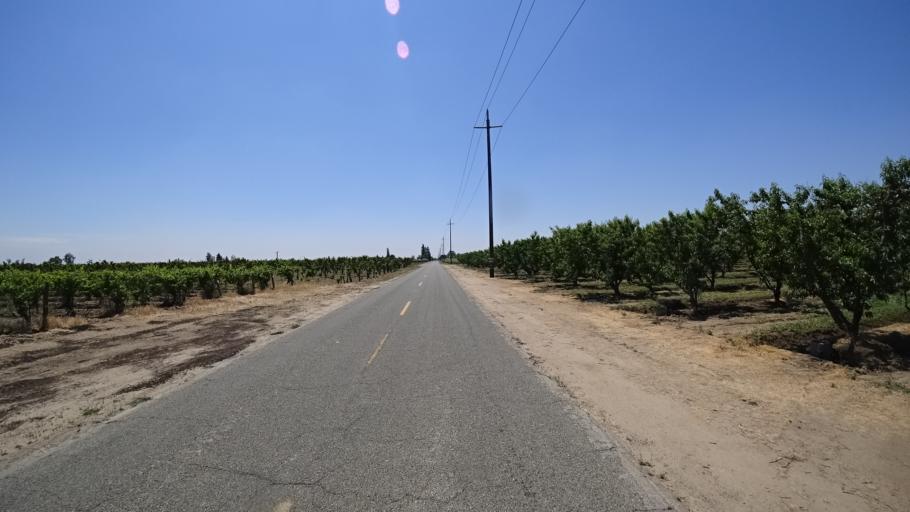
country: US
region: California
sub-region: Fresno County
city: Kingsburg
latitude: 36.4791
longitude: -119.5821
